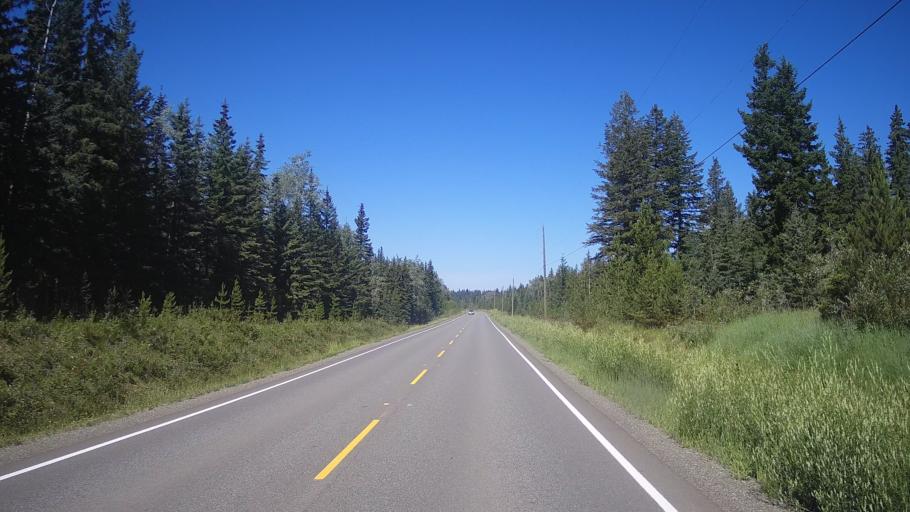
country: CA
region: British Columbia
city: Cache Creek
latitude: 51.5442
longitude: -121.0647
